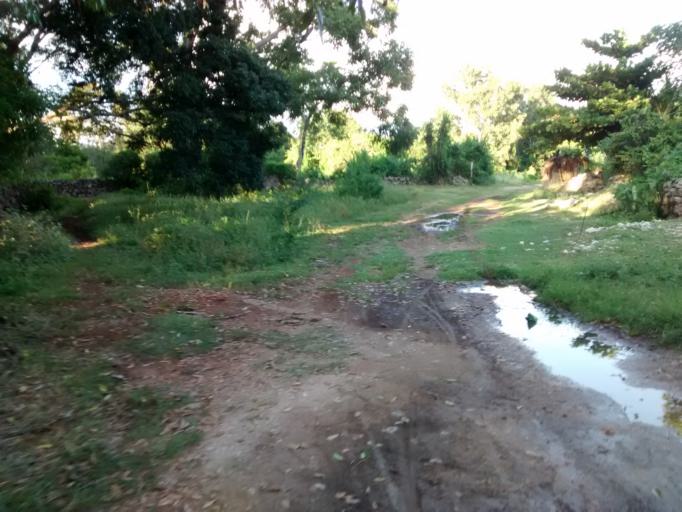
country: MX
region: Yucatan
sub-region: Valladolid
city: Dzitnup
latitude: 20.6483
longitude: -88.2433
